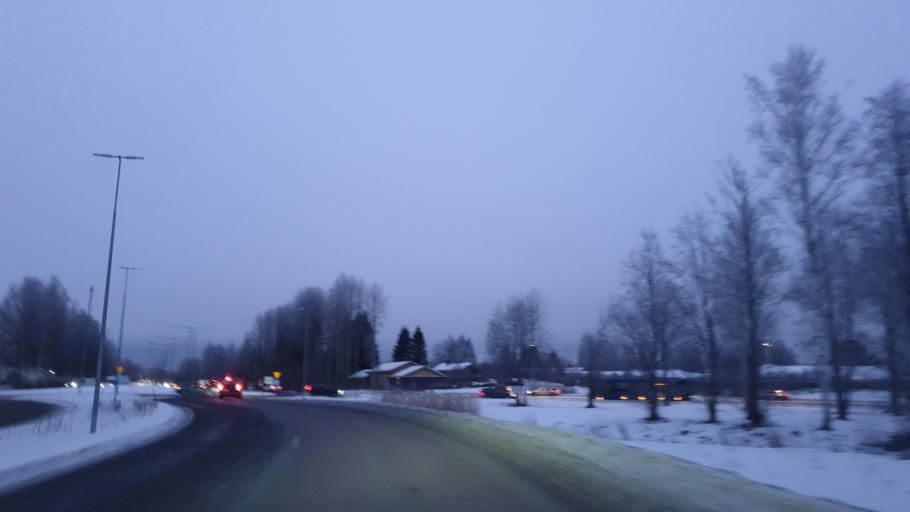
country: SE
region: Vaesterbotten
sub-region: Umea Kommun
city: Umea
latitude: 63.8108
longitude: 20.2490
